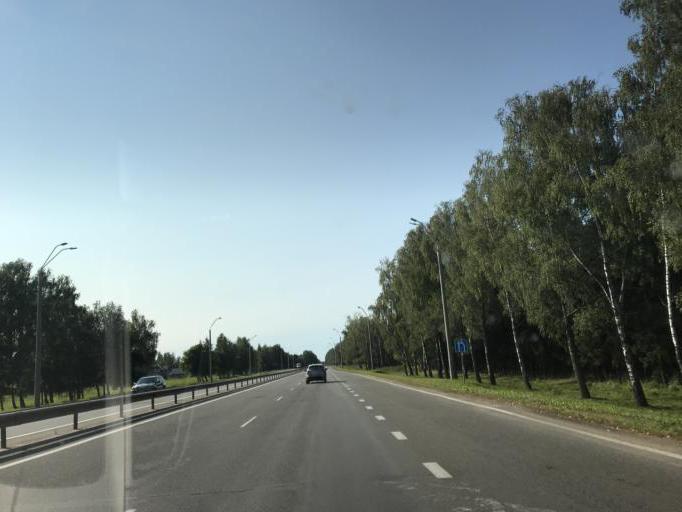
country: BY
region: Mogilev
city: Buynichy
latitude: 53.8549
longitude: 30.2550
